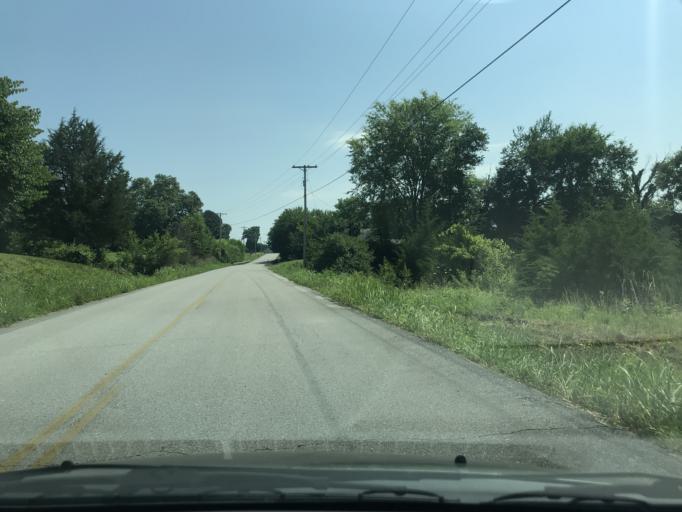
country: US
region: Tennessee
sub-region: Loudon County
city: Loudon
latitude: 35.8128
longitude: -84.3424
